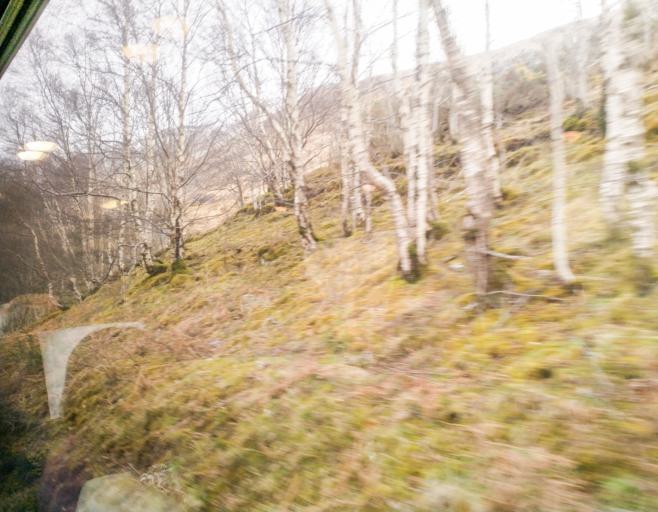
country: GB
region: Scotland
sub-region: Highland
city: Spean Bridge
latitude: 56.8181
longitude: -4.7140
